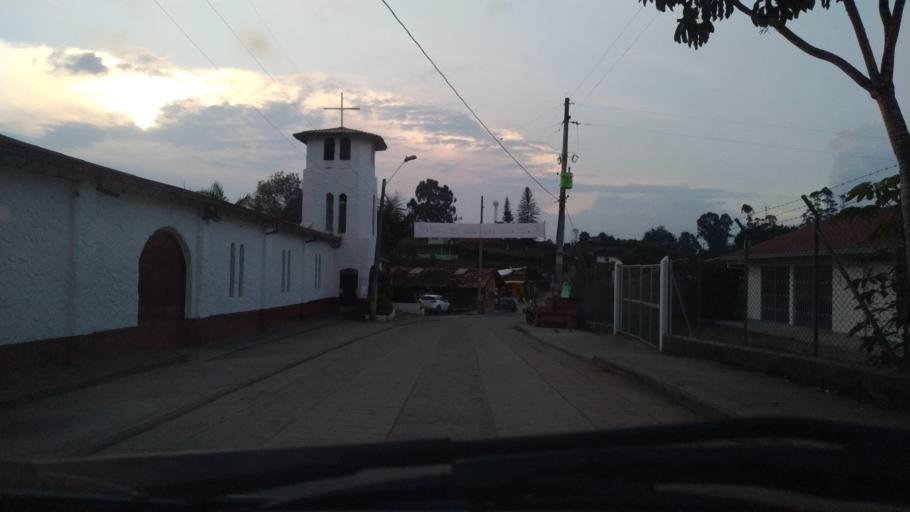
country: CO
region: Antioquia
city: Marinilla
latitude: 6.1938
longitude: -75.2866
